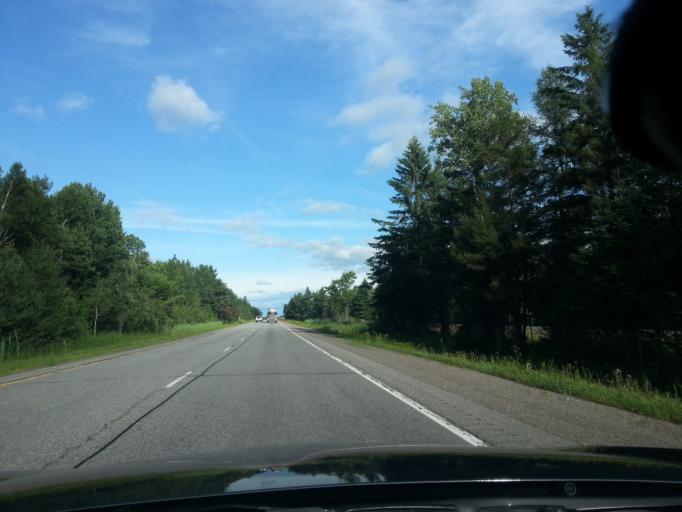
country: CA
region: Quebec
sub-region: Laurentides
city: Brownsburg-Chatham
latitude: 45.5576
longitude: -74.4678
